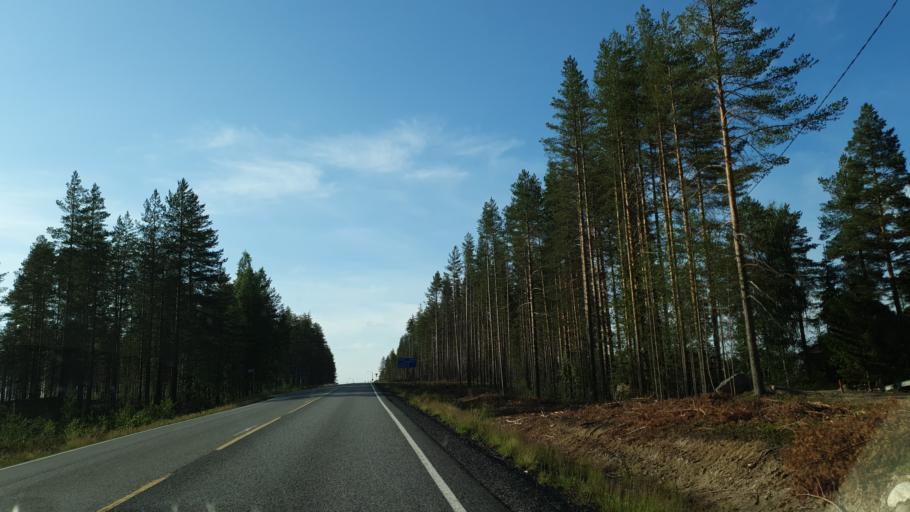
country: FI
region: Kainuu
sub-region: Kehys-Kainuu
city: Kuhmo
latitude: 64.0955
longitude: 29.4775
